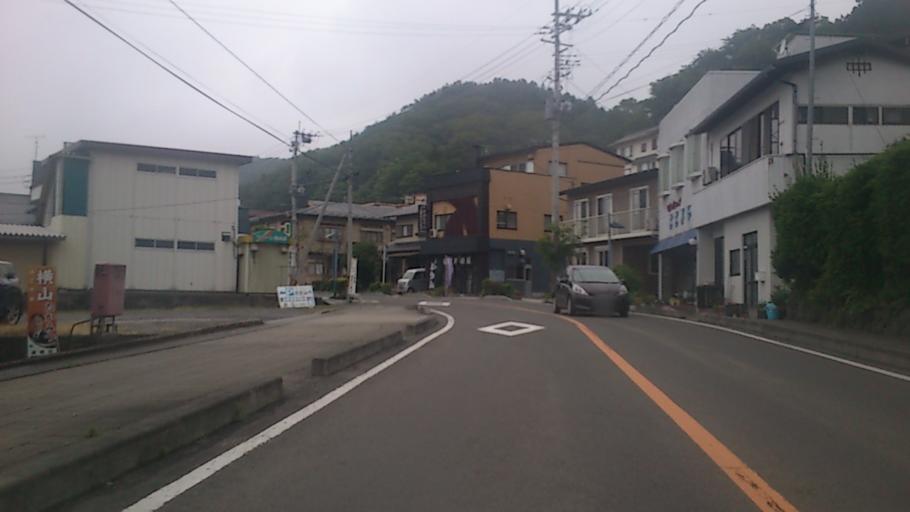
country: JP
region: Miyagi
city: Shiroishi
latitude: 38.1232
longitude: 140.5796
